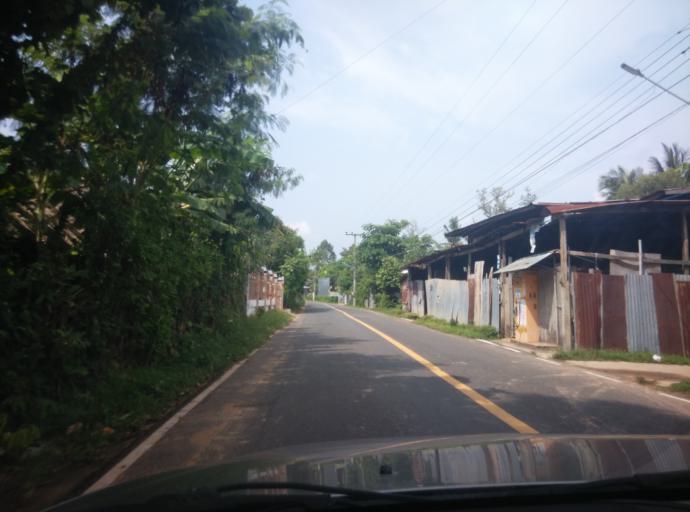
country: TH
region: Sisaket
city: Huai Thap Than
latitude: 15.0302
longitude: 104.0747
